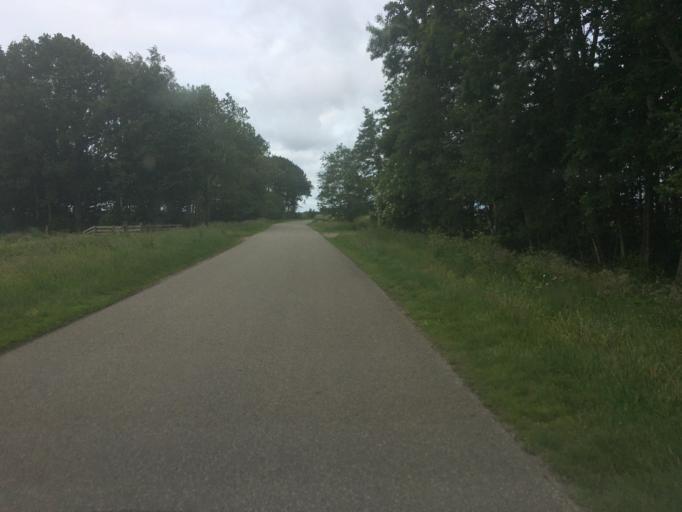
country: NL
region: Friesland
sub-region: Gemeente Skarsterlan
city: Oudehaske
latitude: 52.9027
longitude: 5.8850
